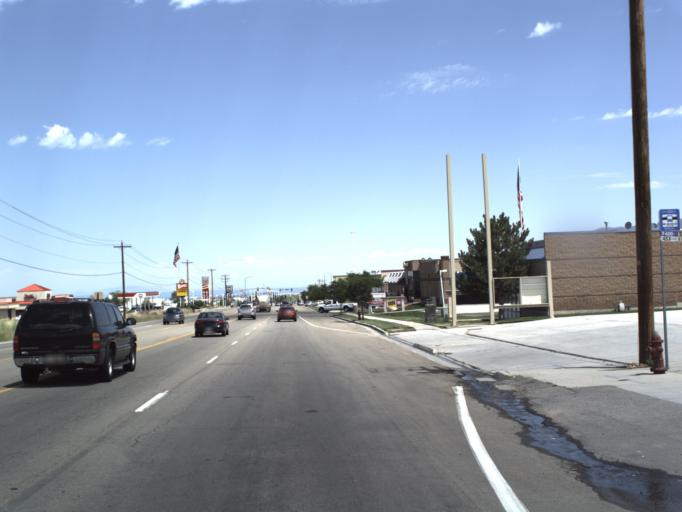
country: US
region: Utah
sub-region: Tooele County
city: Tooele
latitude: 40.5448
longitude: -112.2982
